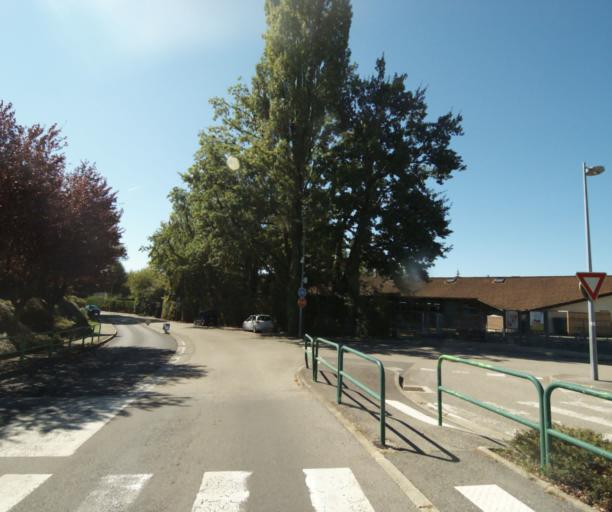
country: FR
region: Rhone-Alpes
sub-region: Departement de l'Ain
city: Ferney-Voltaire
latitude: 46.2530
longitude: 6.0970
